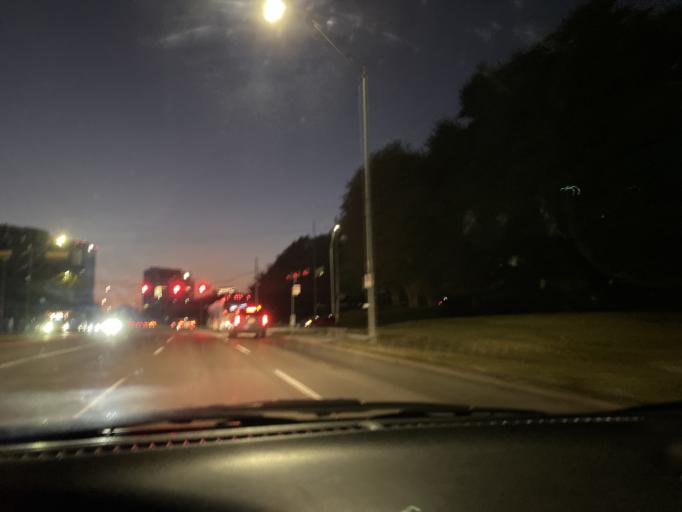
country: US
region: Texas
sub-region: Harris County
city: Bunker Hill Village
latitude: 29.7289
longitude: -95.5484
